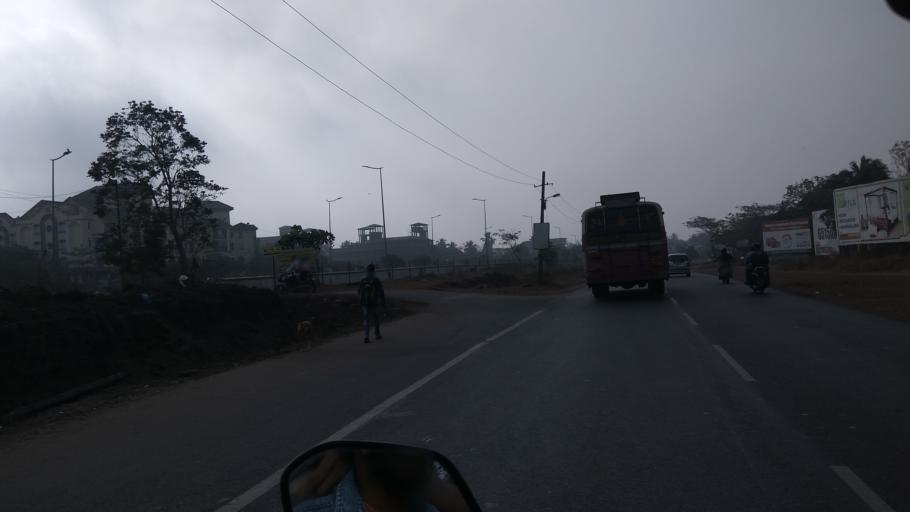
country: IN
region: Goa
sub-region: North Goa
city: Panaji
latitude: 15.5232
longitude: 73.8285
